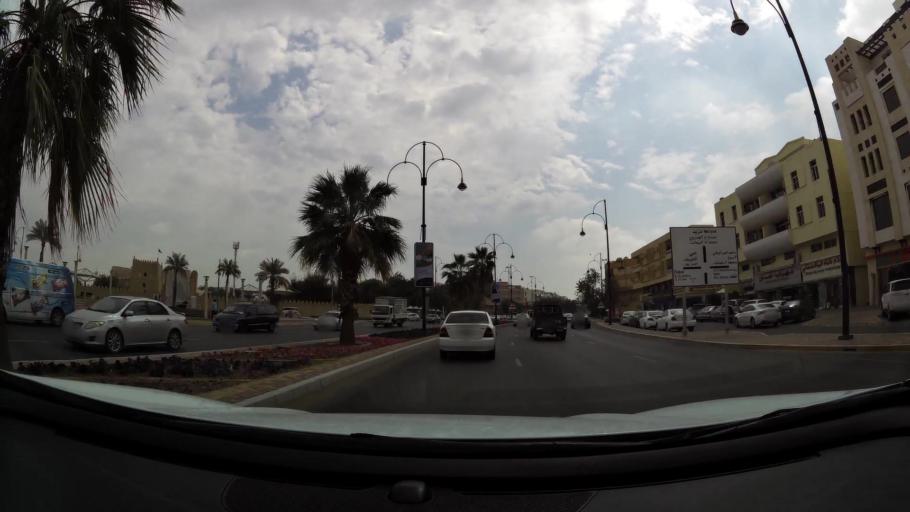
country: AE
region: Abu Dhabi
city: Al Ain
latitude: 24.2208
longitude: 55.7737
